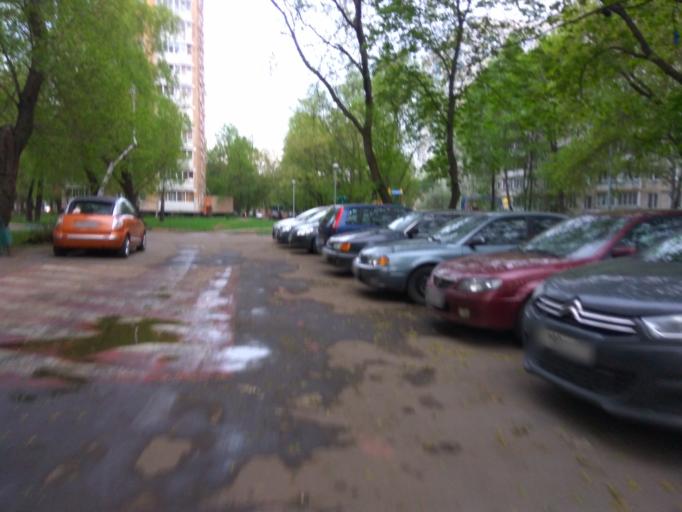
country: RU
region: Moskovskaya
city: Novogireyevo
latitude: 55.7467
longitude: 37.8139
